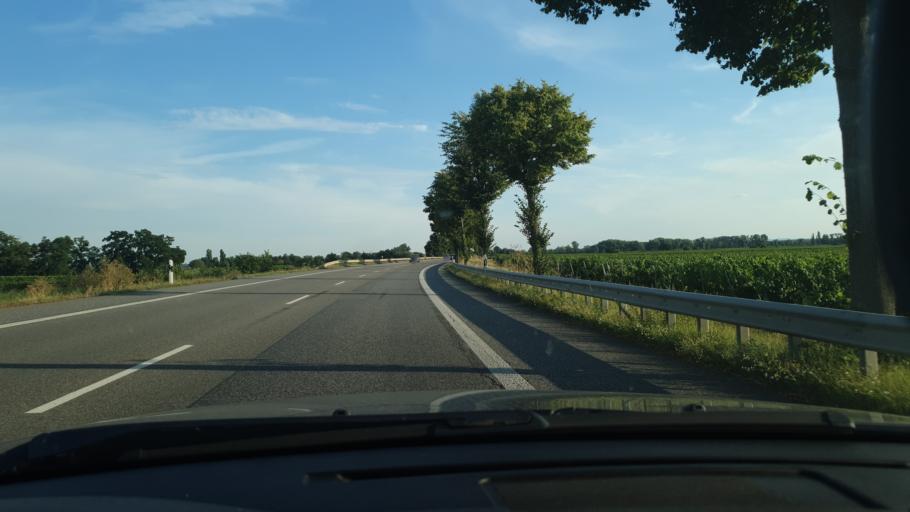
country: DE
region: Rheinland-Pfalz
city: Mettenheim
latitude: 49.7430
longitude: 8.3518
